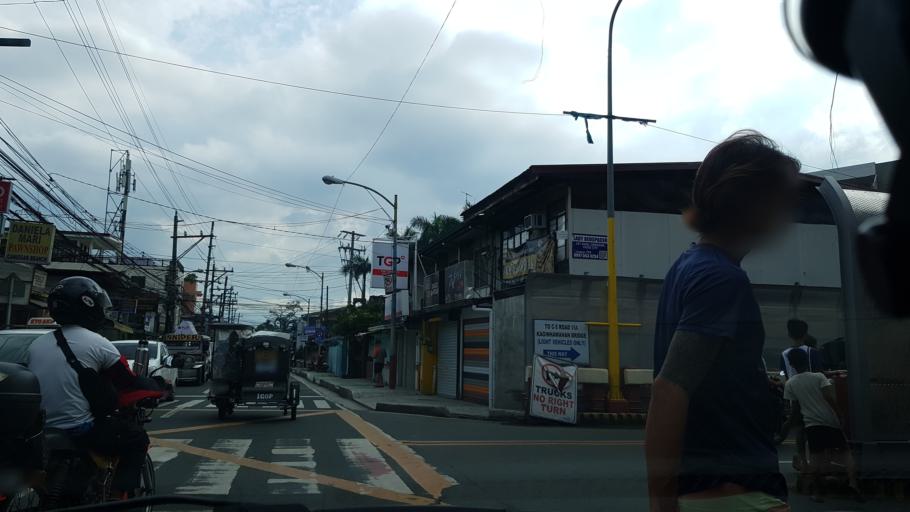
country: PH
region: Metro Manila
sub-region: Pasig
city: Pasig City
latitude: 14.5737
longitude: 121.0786
